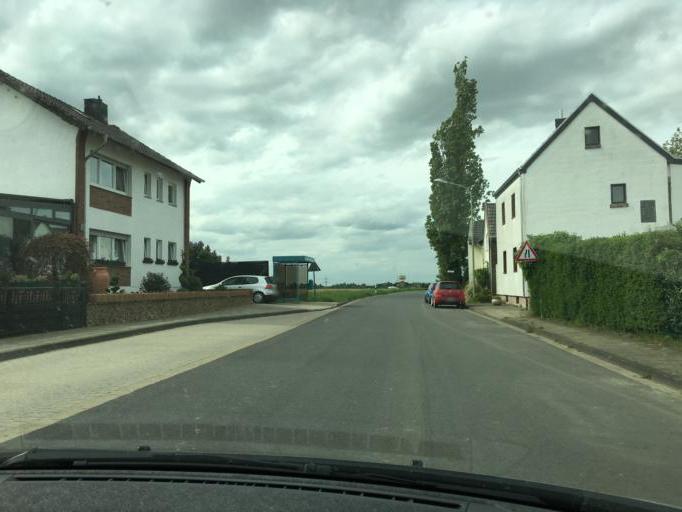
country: DE
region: North Rhine-Westphalia
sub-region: Regierungsbezirk Koln
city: Merzenich
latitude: 50.7849
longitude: 6.5499
